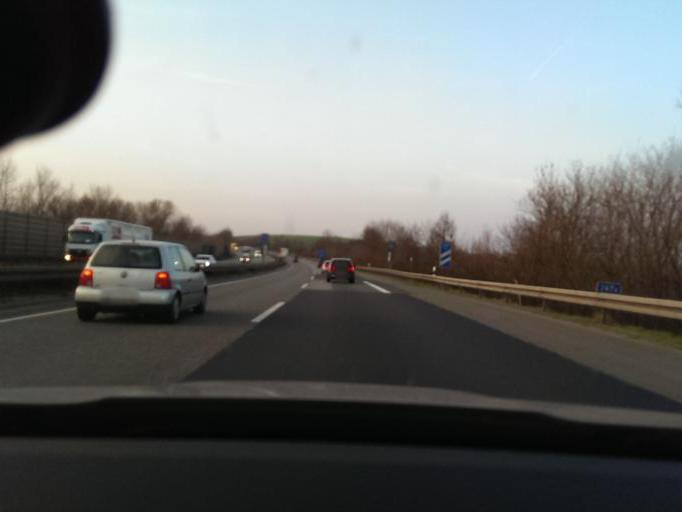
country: DE
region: Lower Saxony
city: Hillerse
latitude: 51.6963
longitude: 9.9370
